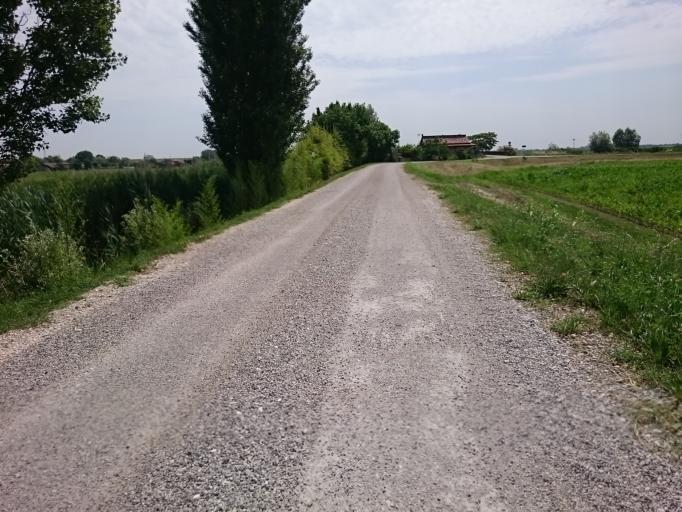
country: IT
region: Veneto
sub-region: Provincia di Venezia
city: Valli
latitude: 45.2211
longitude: 12.1541
